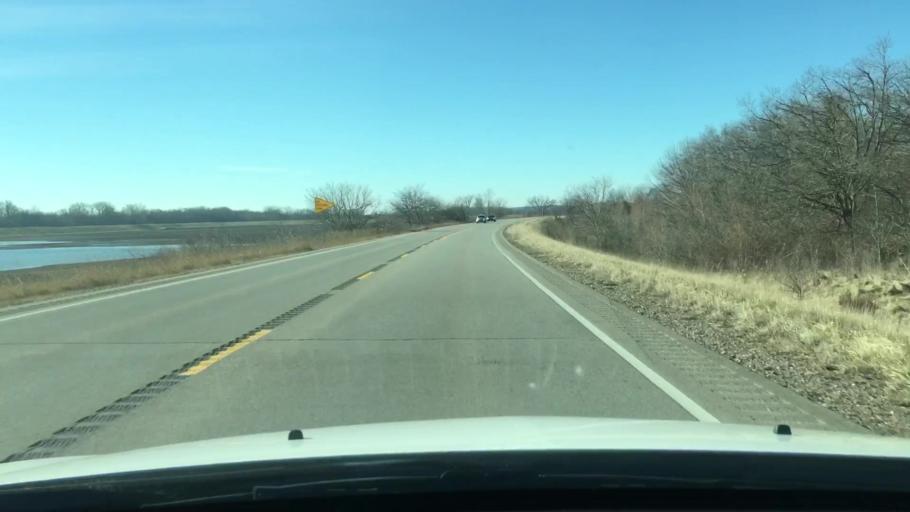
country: US
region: Illinois
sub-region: Peoria County
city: Glasford
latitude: 40.5538
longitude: -89.7899
